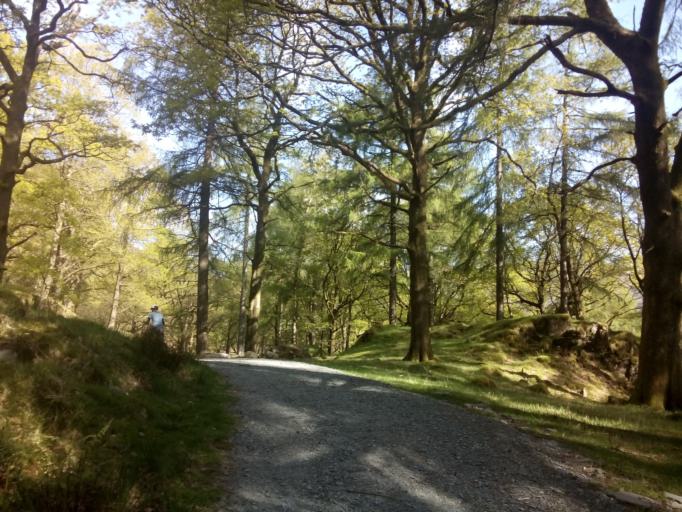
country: GB
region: England
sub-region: Cumbria
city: Ambleside
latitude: 54.4369
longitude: -3.0652
